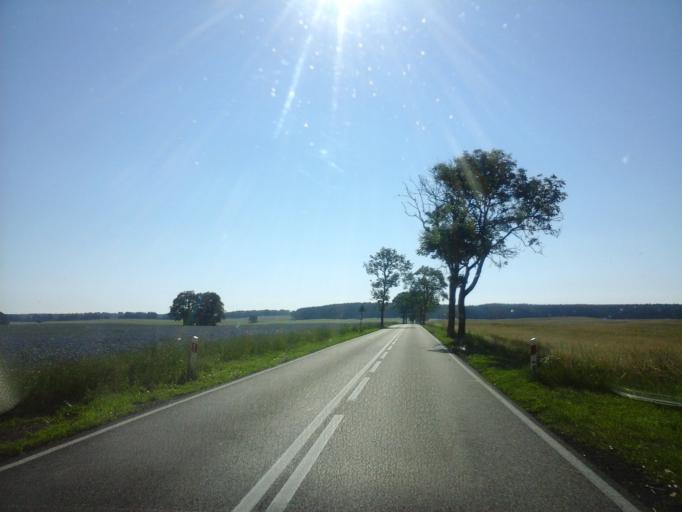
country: PL
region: West Pomeranian Voivodeship
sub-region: Powiat lobeski
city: Wegorzyno
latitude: 53.4977
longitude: 15.6795
